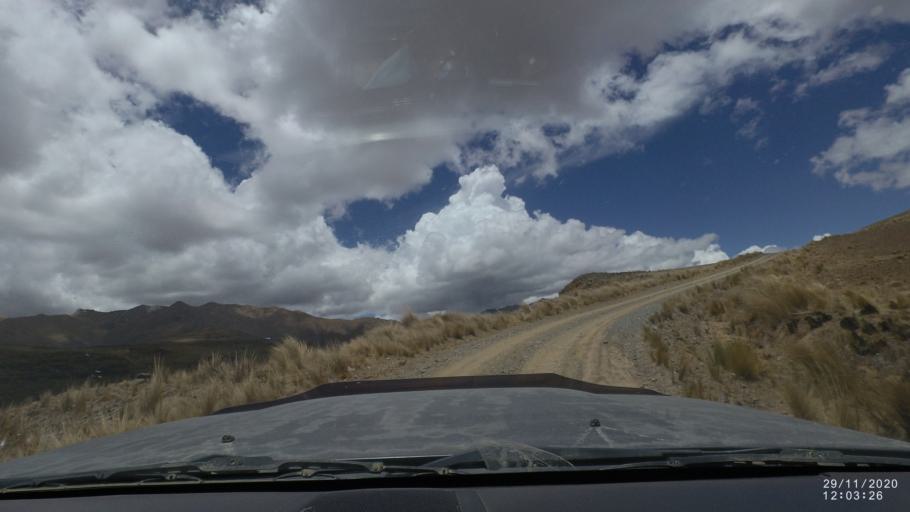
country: BO
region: Cochabamba
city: Cochabamba
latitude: -17.1505
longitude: -66.2856
